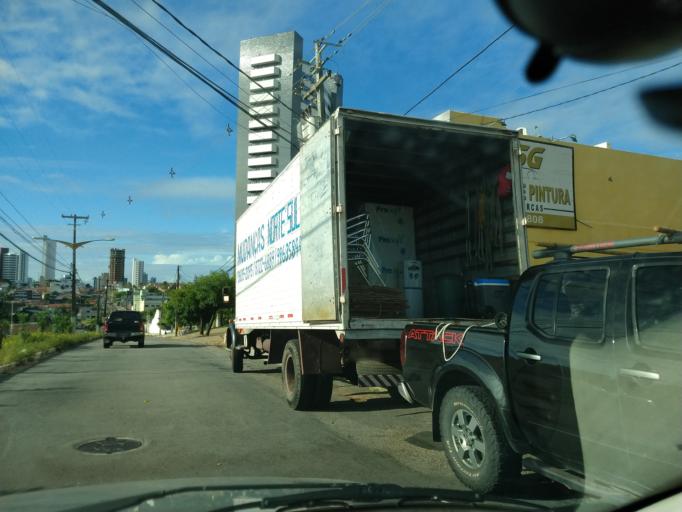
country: BR
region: Rio Grande do Norte
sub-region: Natal
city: Natal
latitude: -5.8355
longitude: -35.2246
